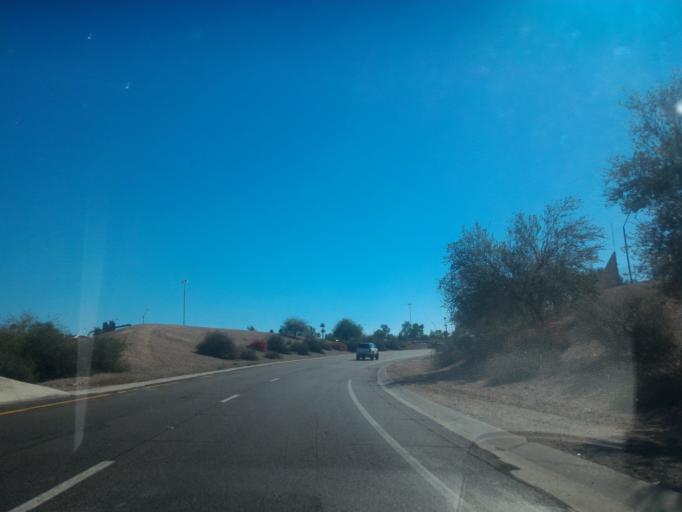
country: US
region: Arizona
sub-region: Maricopa County
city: Tempe
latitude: 33.3840
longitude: -111.8923
